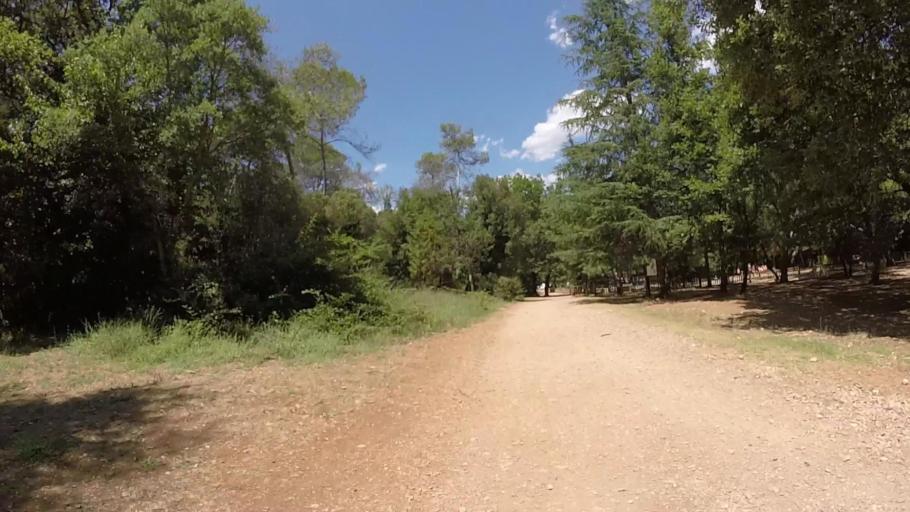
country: FR
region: Provence-Alpes-Cote d'Azur
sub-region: Departement des Alpes-Maritimes
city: Le Cannet
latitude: 43.5991
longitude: 7.0290
